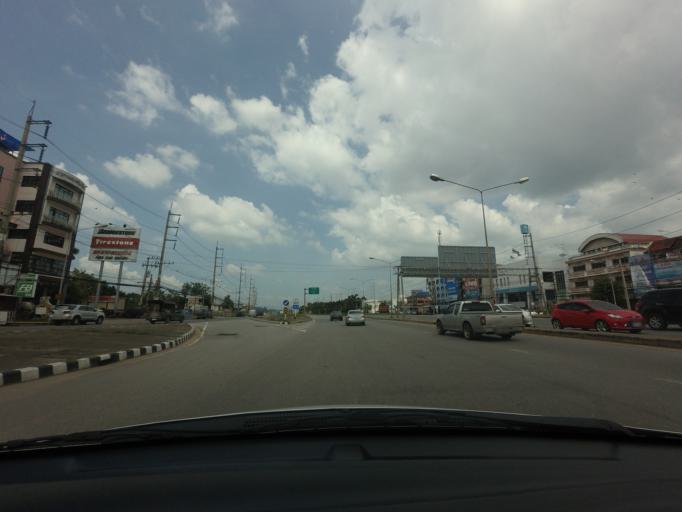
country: TH
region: Prachin Buri
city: Kabin Buri
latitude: 13.9851
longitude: 101.7625
